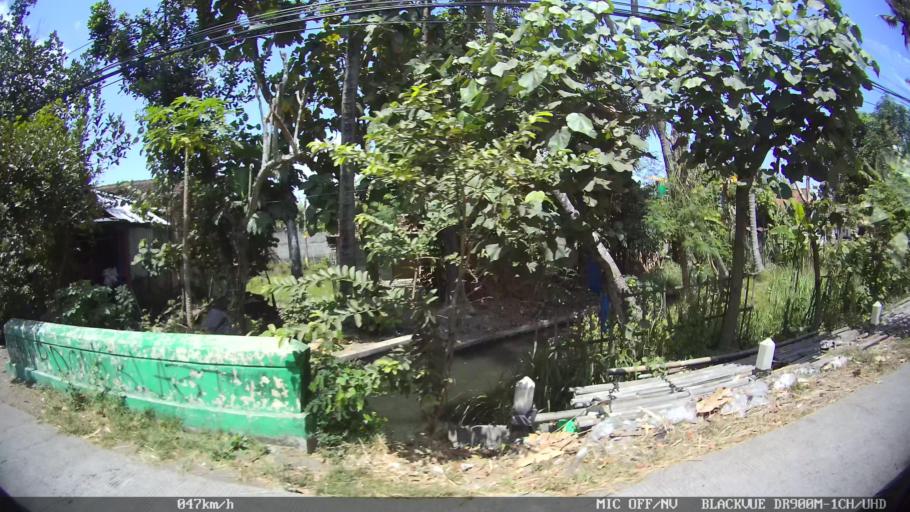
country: ID
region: Daerah Istimewa Yogyakarta
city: Pundong
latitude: -7.9204
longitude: 110.3763
